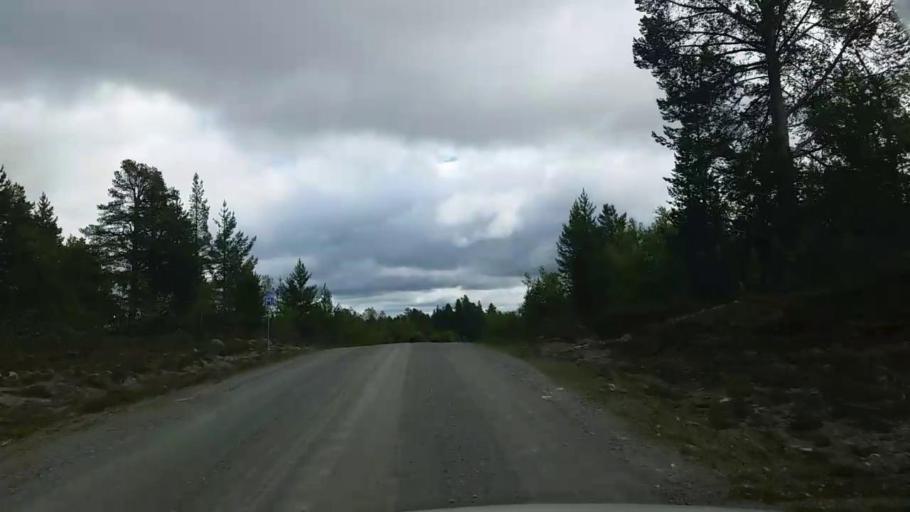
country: NO
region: Hedmark
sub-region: Engerdal
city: Engerdal
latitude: 62.3463
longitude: 12.5940
